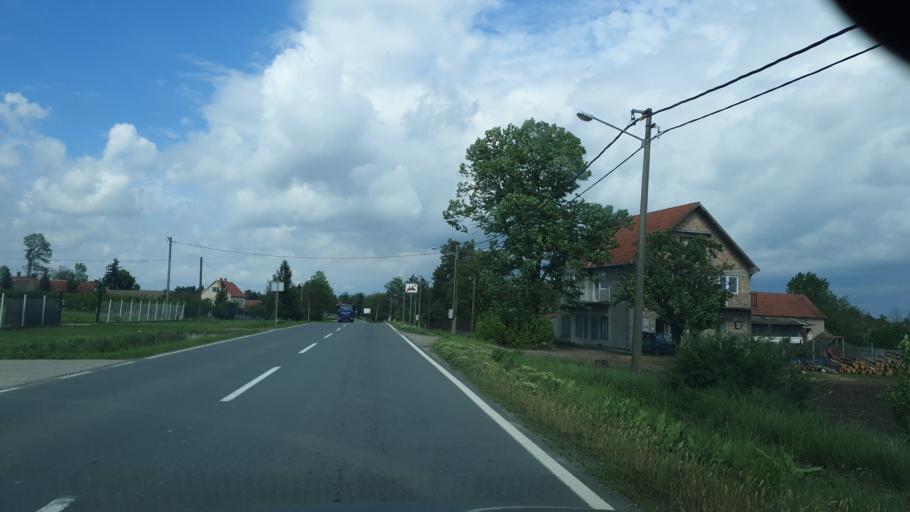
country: RS
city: Stubline
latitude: 44.5514
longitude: 20.1429
